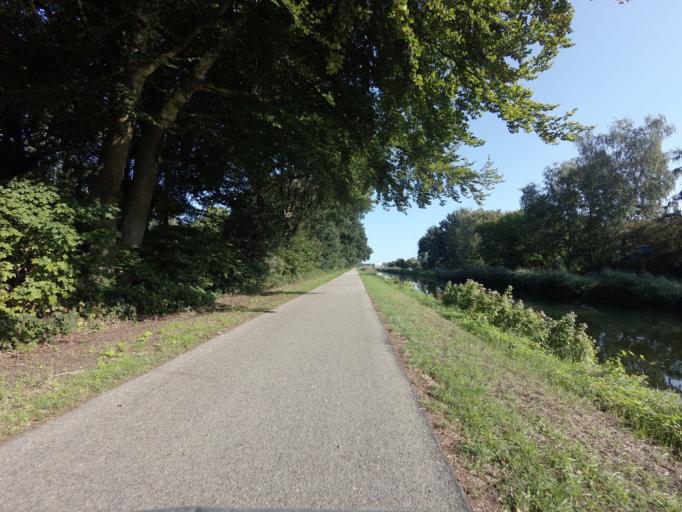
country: NL
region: Overijssel
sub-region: Gemeente Raalte
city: Raalte
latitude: 52.3757
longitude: 6.2780
